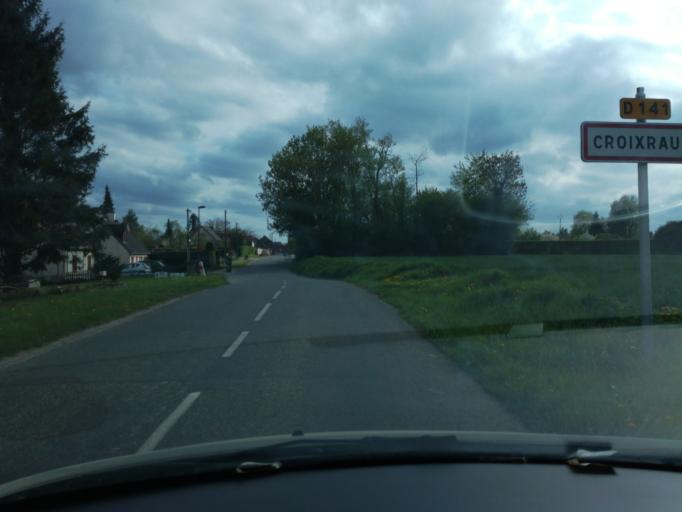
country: FR
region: Picardie
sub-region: Departement de la Somme
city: Poix-de-Picardie
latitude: 49.7952
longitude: 1.9934
